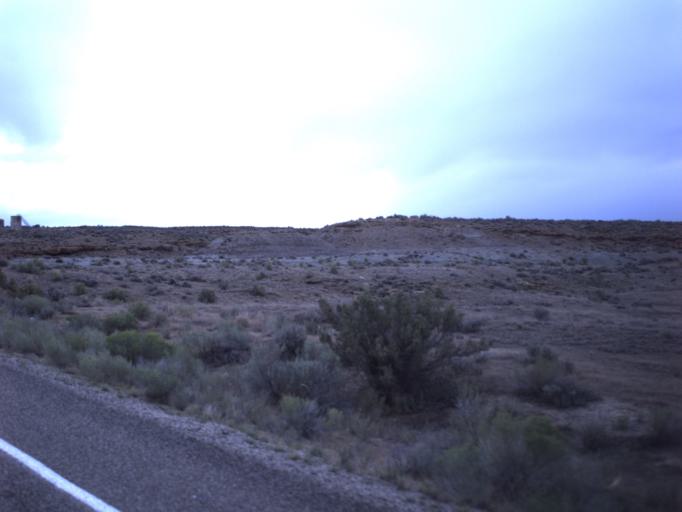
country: US
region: Colorado
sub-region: Rio Blanco County
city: Rangely
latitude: 40.0745
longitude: -109.2069
